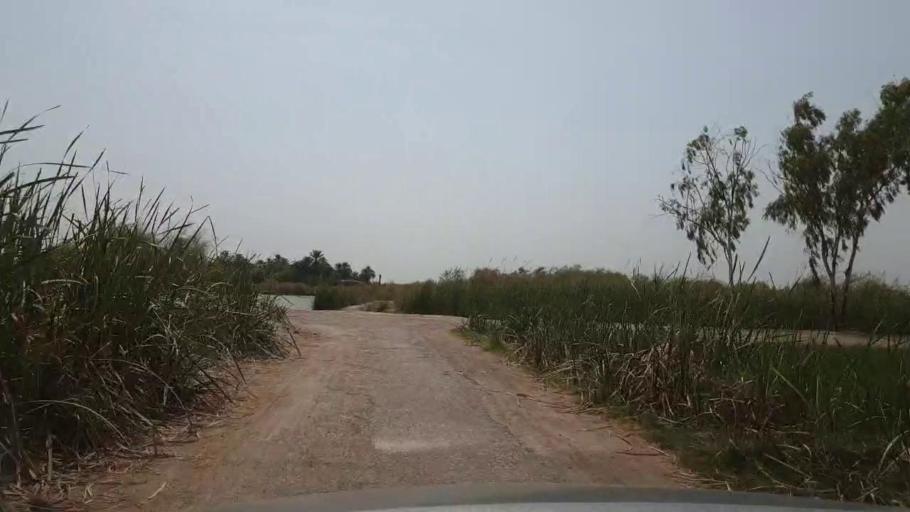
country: PK
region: Sindh
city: Garhi Yasin
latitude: 27.8916
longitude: 68.4669
